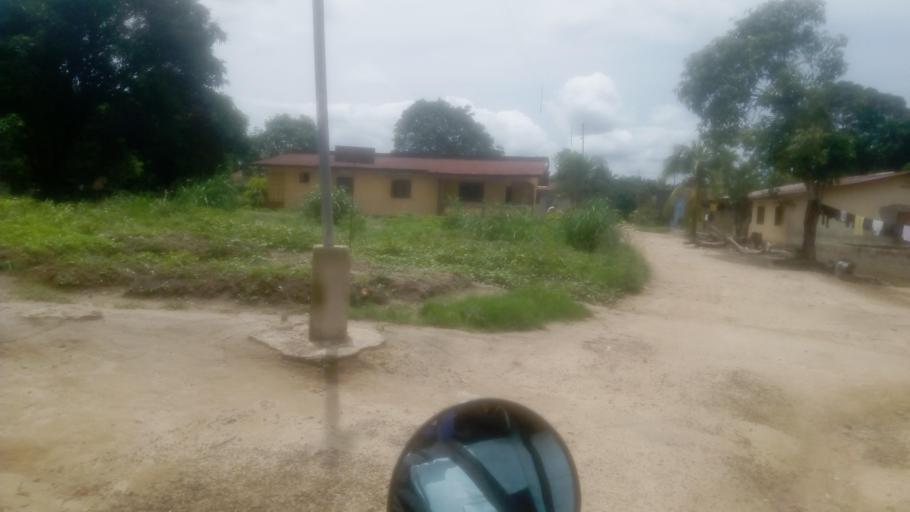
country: SL
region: Southern Province
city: Bo
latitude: 7.9532
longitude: -11.7107
